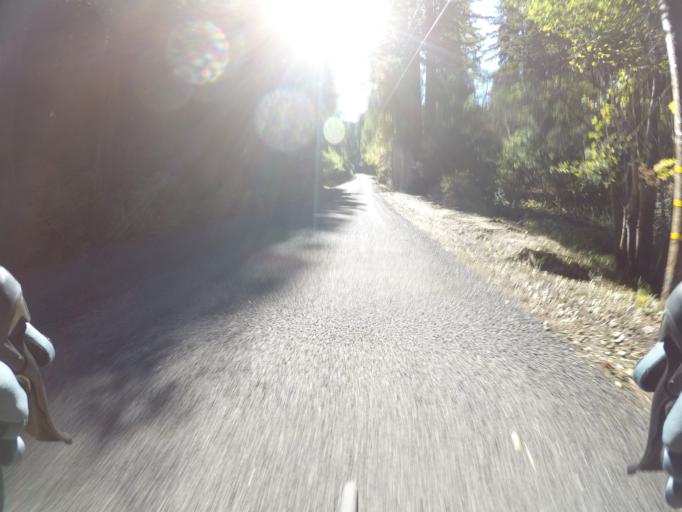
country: US
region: California
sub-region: Santa Cruz County
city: Lompico
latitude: 37.1127
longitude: -122.0206
